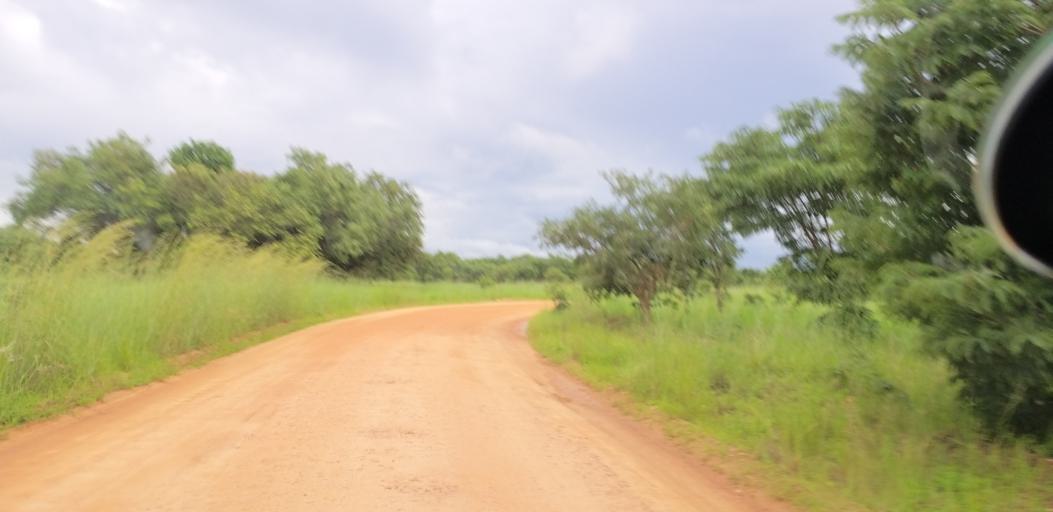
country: ZM
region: Lusaka
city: Chongwe
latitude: -15.1764
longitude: 28.4638
